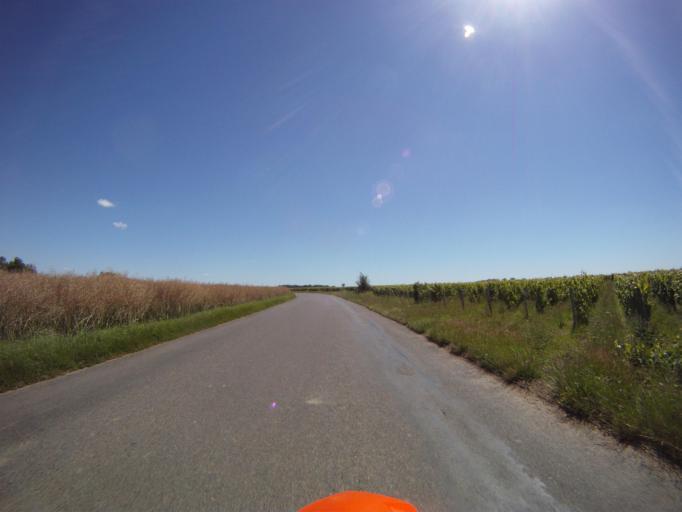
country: FR
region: Centre
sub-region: Departement d'Indre-et-Loire
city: Vouvray
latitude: 47.4426
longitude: 0.8004
